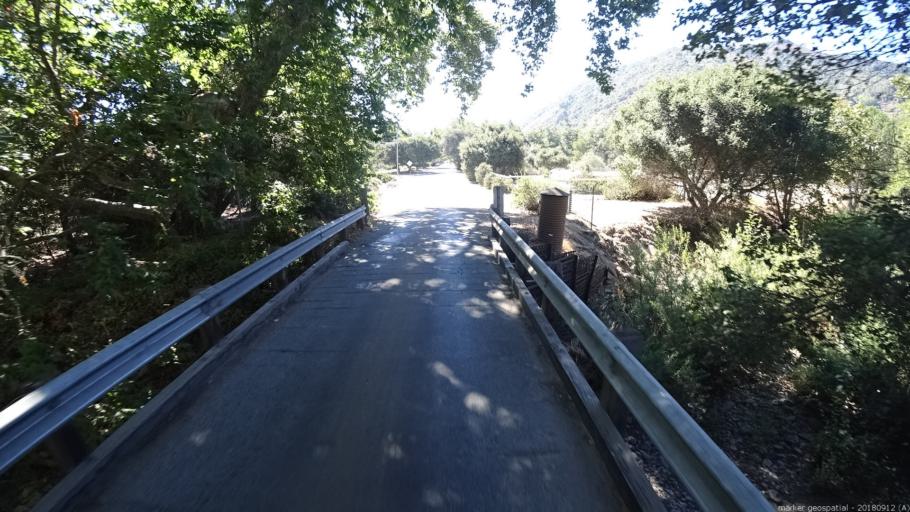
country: US
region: California
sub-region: Monterey County
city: Carmel Valley Village
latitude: 36.4912
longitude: -121.7515
